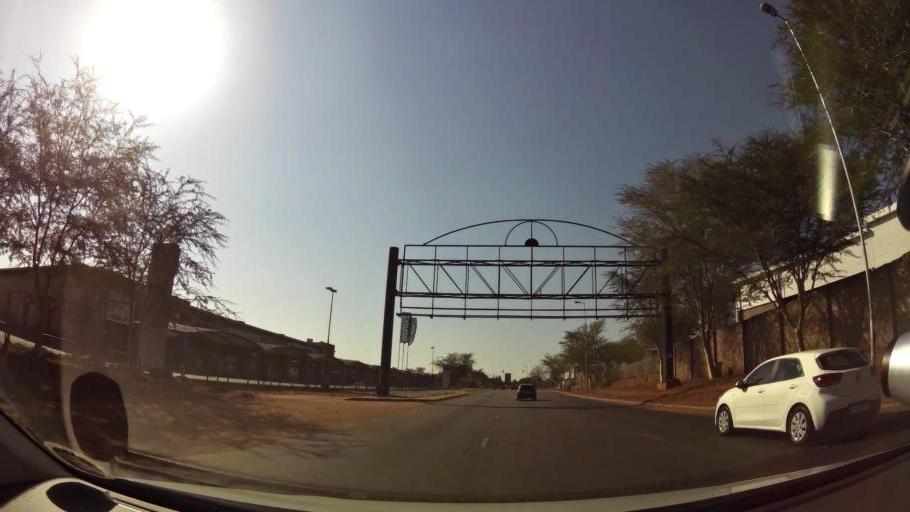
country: ZA
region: Gauteng
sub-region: City of Tshwane Metropolitan Municipality
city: Pretoria
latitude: -25.6798
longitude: 28.1921
